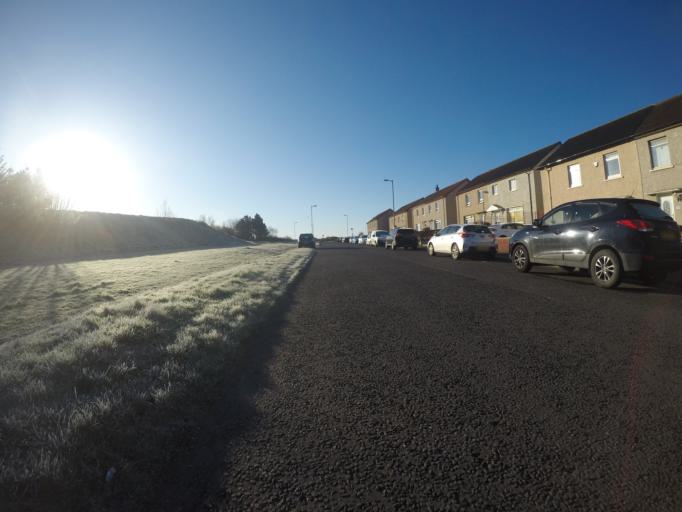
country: GB
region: Scotland
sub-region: North Ayrshire
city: Stevenston
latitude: 55.6307
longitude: -4.7398
